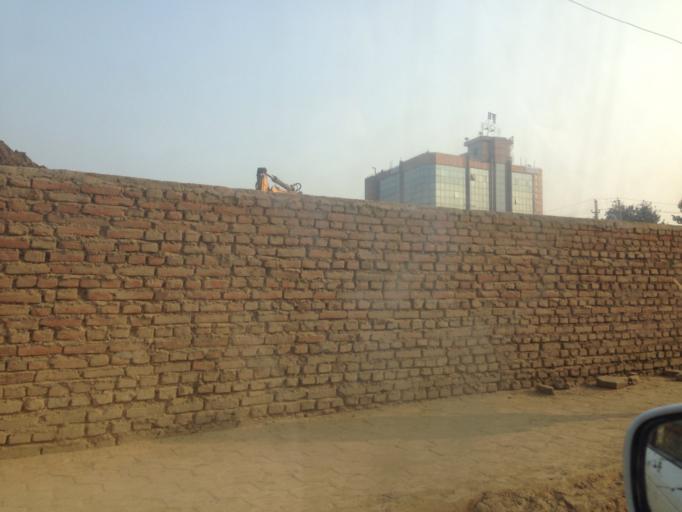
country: NP
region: Central Region
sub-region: Bagmati Zone
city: Kathmandu
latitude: 27.7176
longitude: 85.3142
